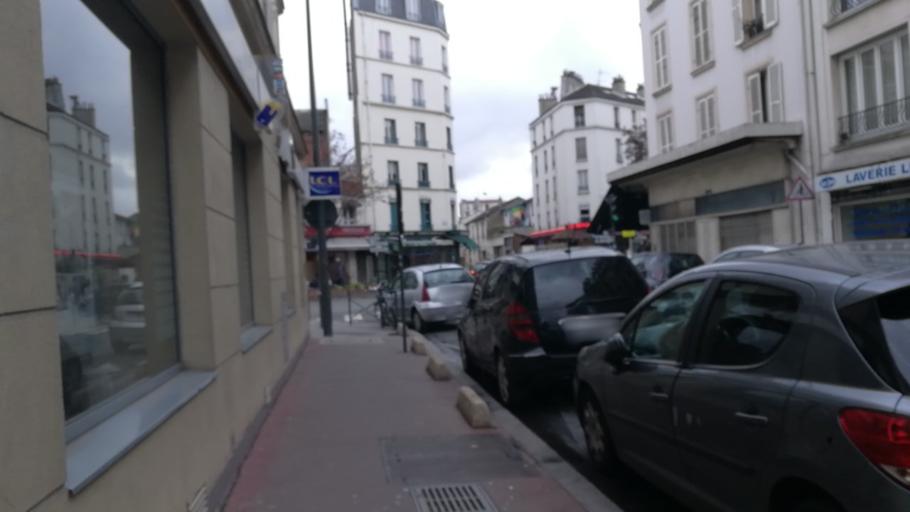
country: FR
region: Ile-de-France
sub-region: Paris
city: Saint-Ouen
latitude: 48.9088
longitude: 2.3322
